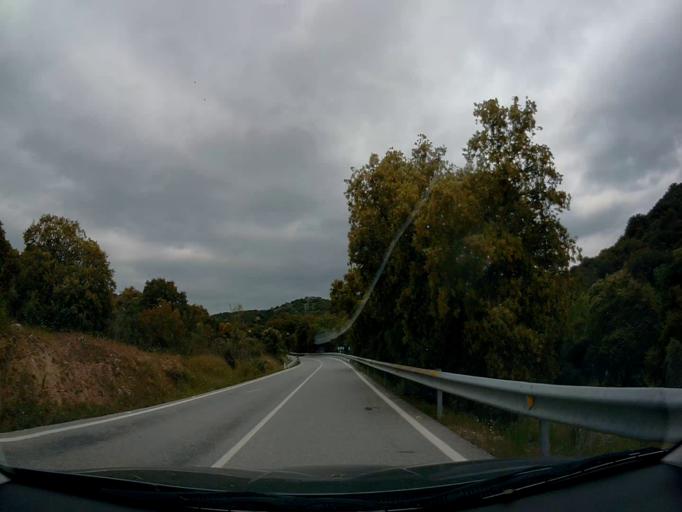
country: ES
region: Madrid
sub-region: Provincia de Madrid
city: Navalagamella
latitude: 40.4349
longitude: -4.1091
